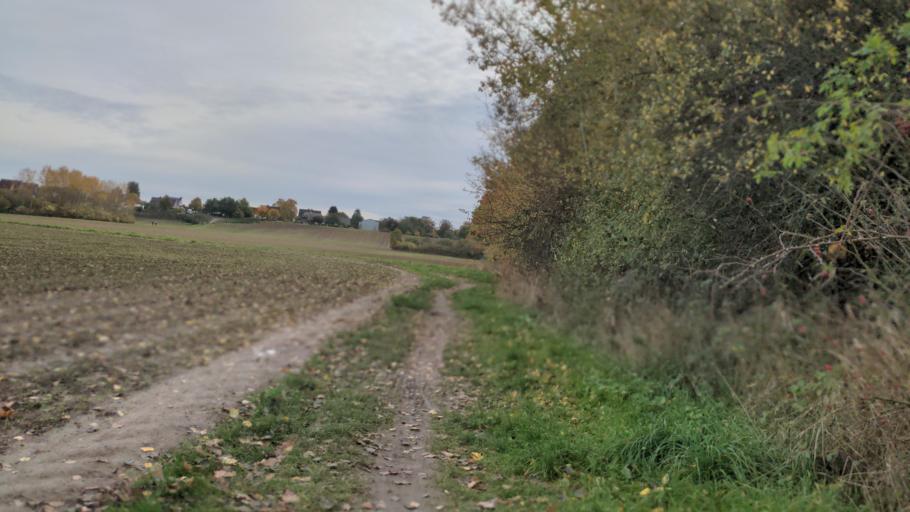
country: DE
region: Schleswig-Holstein
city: Stockelsdorf
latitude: 53.9076
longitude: 10.6539
